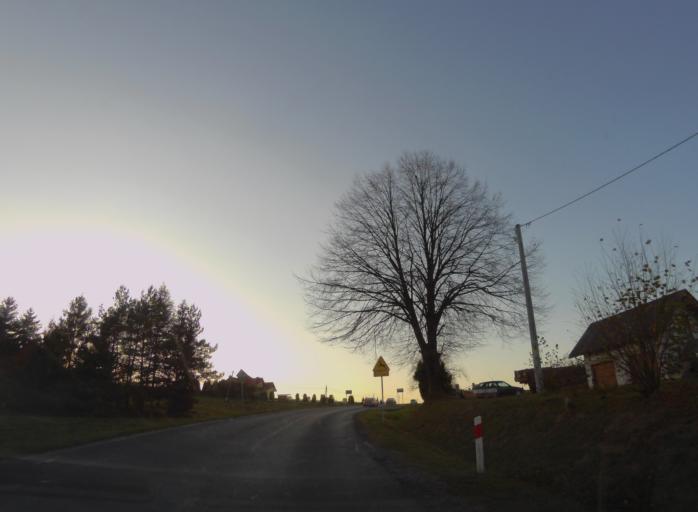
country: PL
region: Subcarpathian Voivodeship
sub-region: Powiat leski
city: Lesko
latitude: 49.4181
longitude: 22.3361
